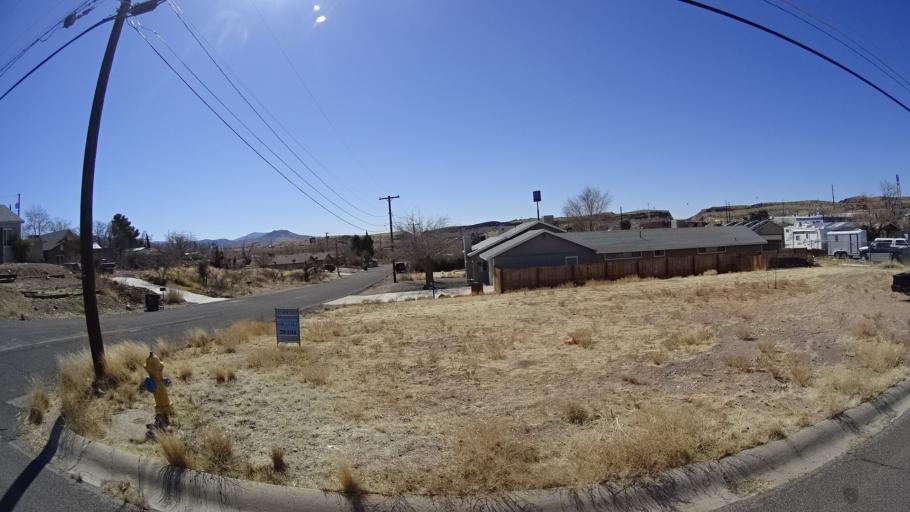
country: US
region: Arizona
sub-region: Mohave County
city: Kingman
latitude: 35.1926
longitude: -114.0625
